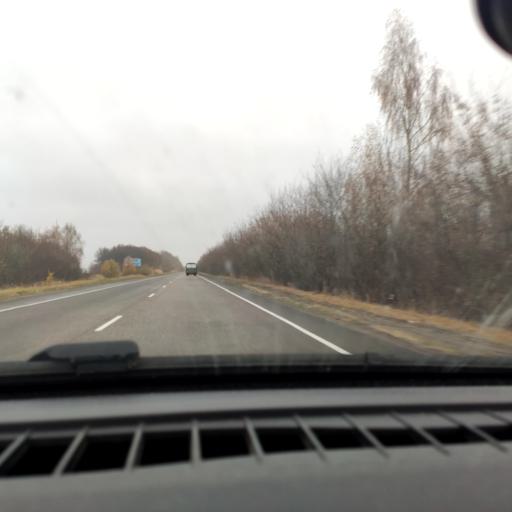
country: RU
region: Voronezj
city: Kolodeznyy
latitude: 51.3509
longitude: 39.0237
